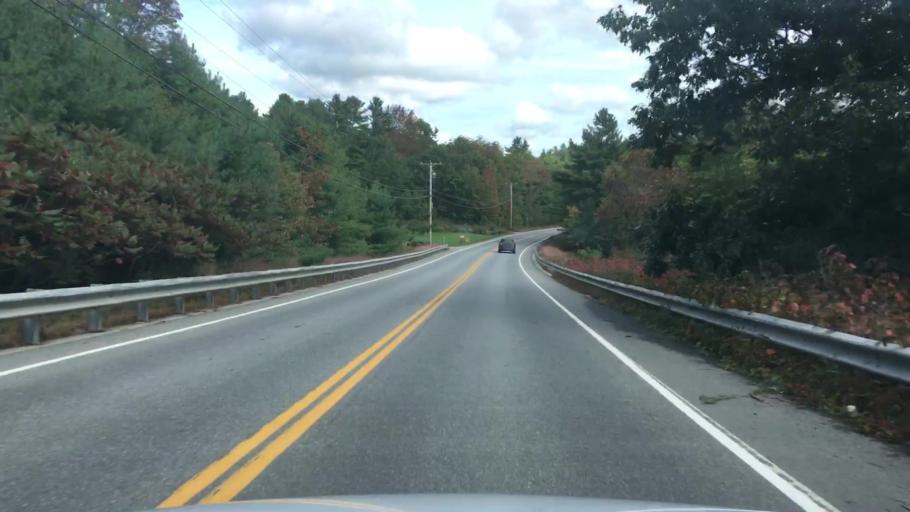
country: US
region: Maine
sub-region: Androscoggin County
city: Lisbon
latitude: 43.9824
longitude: -70.1210
